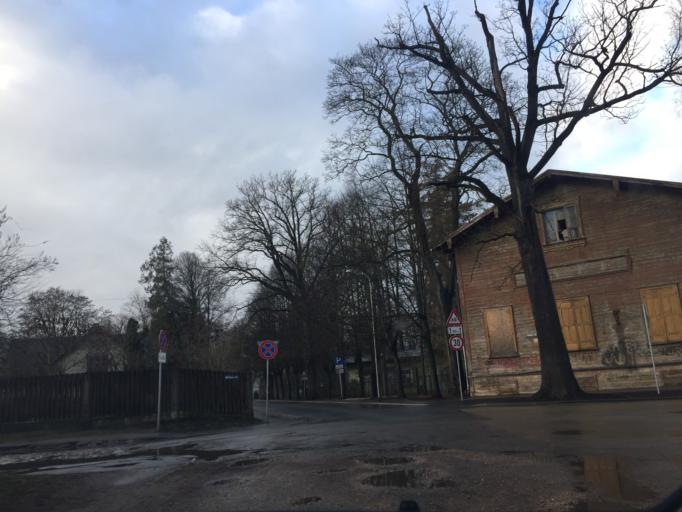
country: LV
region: Marupe
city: Marupe
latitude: 56.9447
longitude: 24.0563
